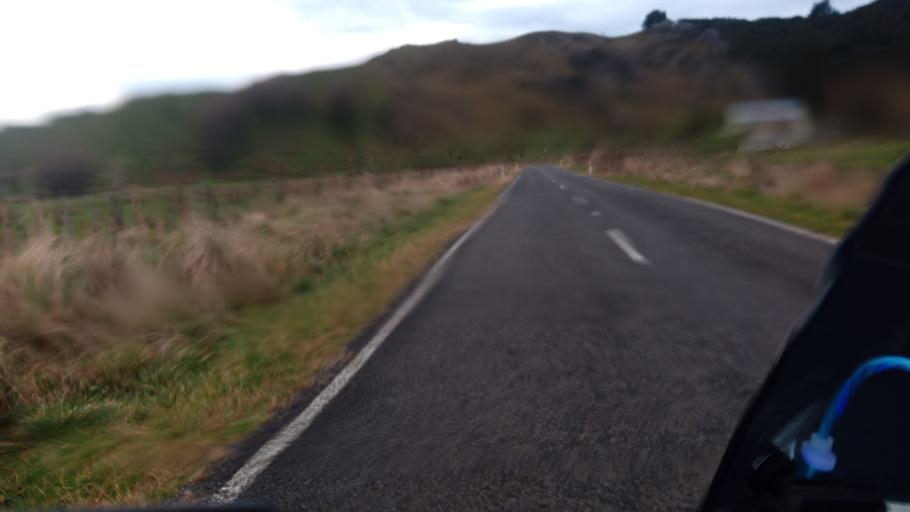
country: NZ
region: Gisborne
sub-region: Gisborne District
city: Gisborne
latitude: -38.3335
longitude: 178.3051
